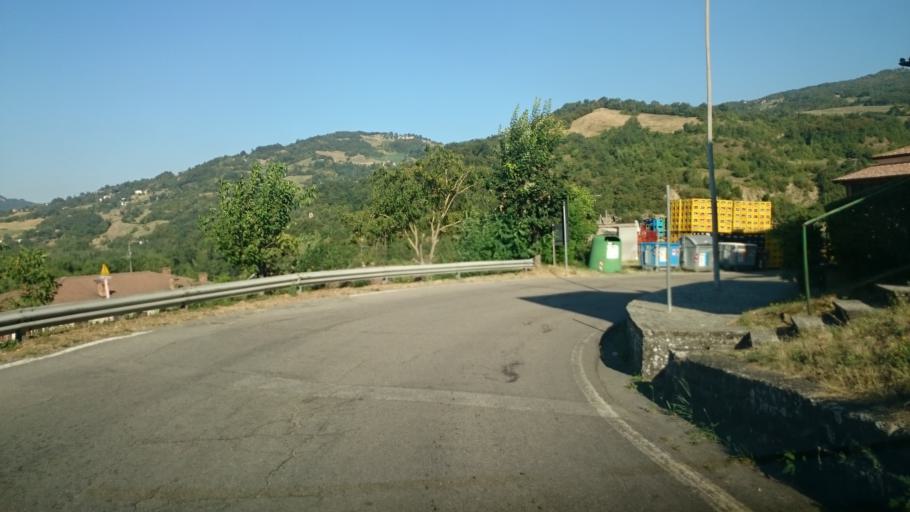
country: IT
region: Emilia-Romagna
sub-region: Provincia di Modena
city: Montefiorino
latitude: 44.4042
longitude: 10.6162
